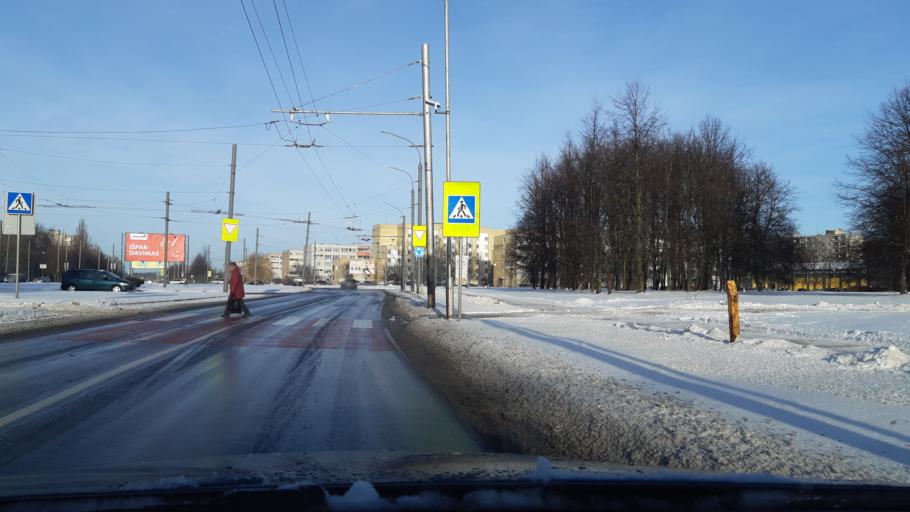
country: LT
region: Kauno apskritis
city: Dainava (Kaunas)
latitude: 54.9221
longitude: 23.9806
